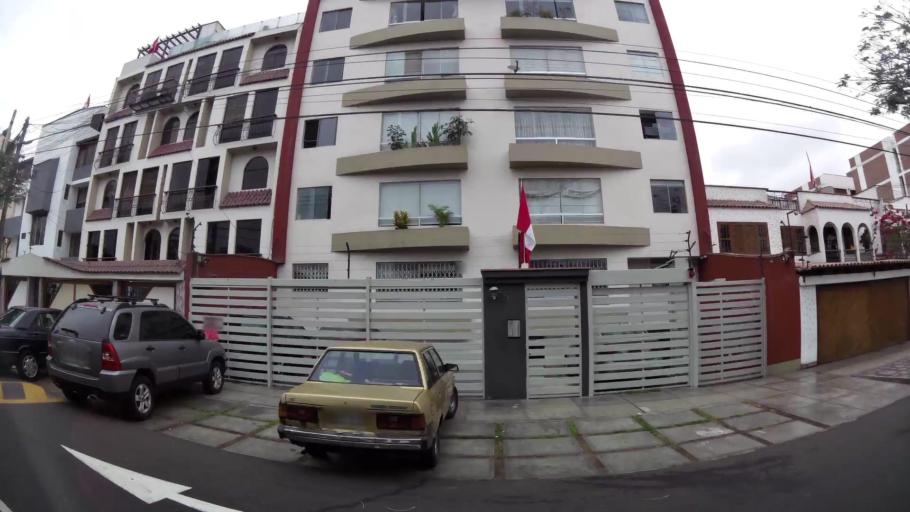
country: PE
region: Lima
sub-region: Lima
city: Surco
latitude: -12.1423
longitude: -76.9958
